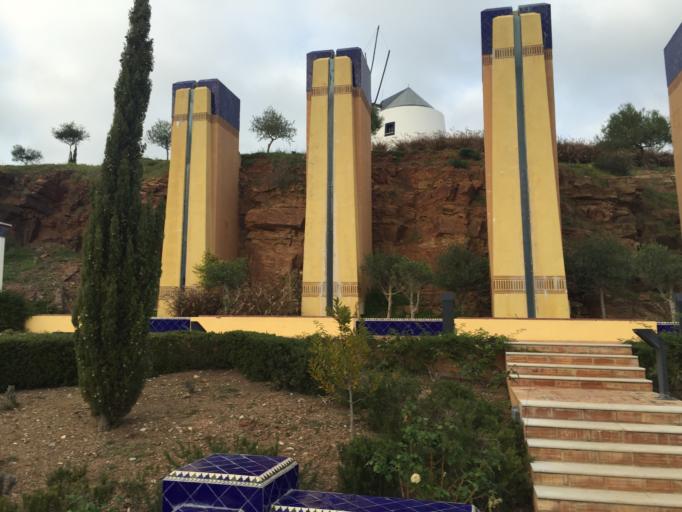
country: PT
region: Faro
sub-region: Castro Marim
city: Castro Marim
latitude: 37.2157
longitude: -7.4398
